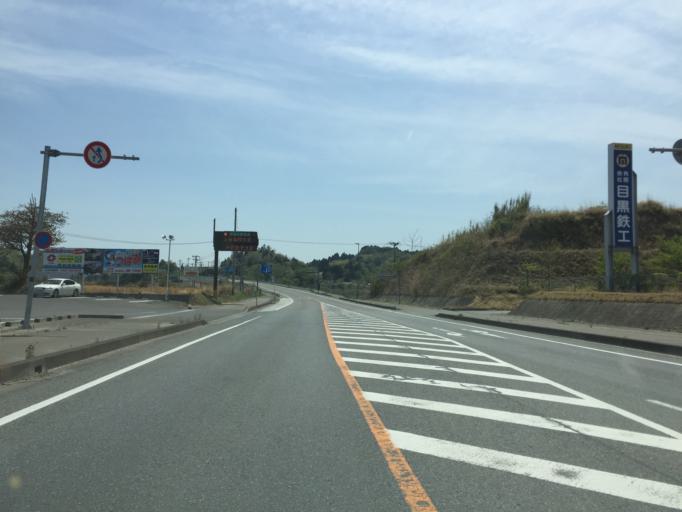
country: JP
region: Miyagi
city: Marumori
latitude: 37.8594
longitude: 140.9200
